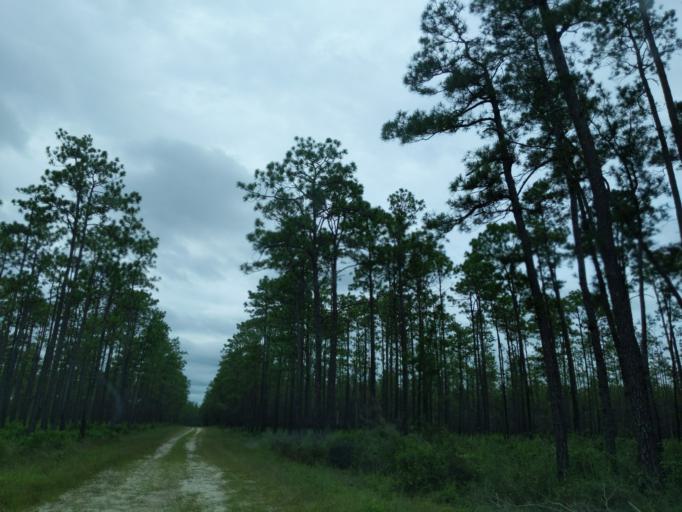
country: US
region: Florida
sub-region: Gadsden County
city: Midway
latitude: 30.3897
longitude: -84.4656
